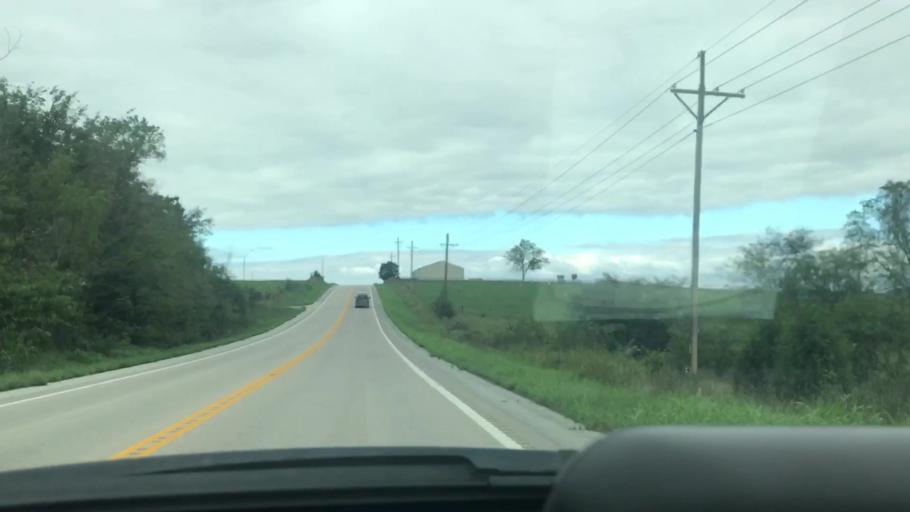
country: US
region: Missouri
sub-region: Hickory County
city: Hermitage
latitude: 37.8815
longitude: -93.1802
